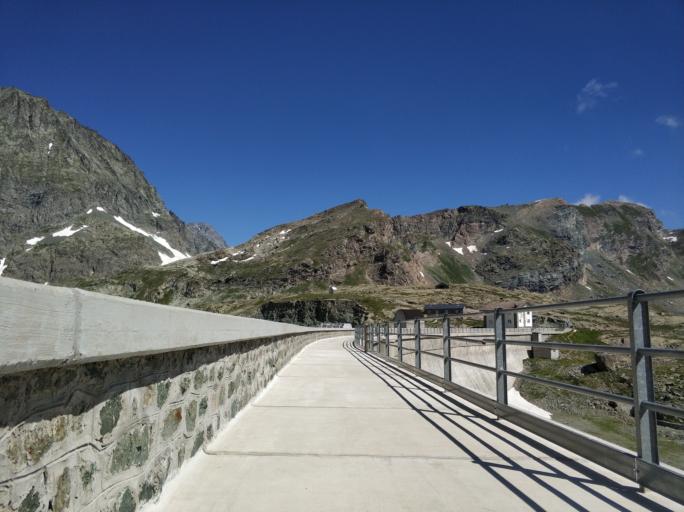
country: IT
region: Piedmont
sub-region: Provincia di Torino
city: Balme
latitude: 45.2684
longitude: 7.1491
